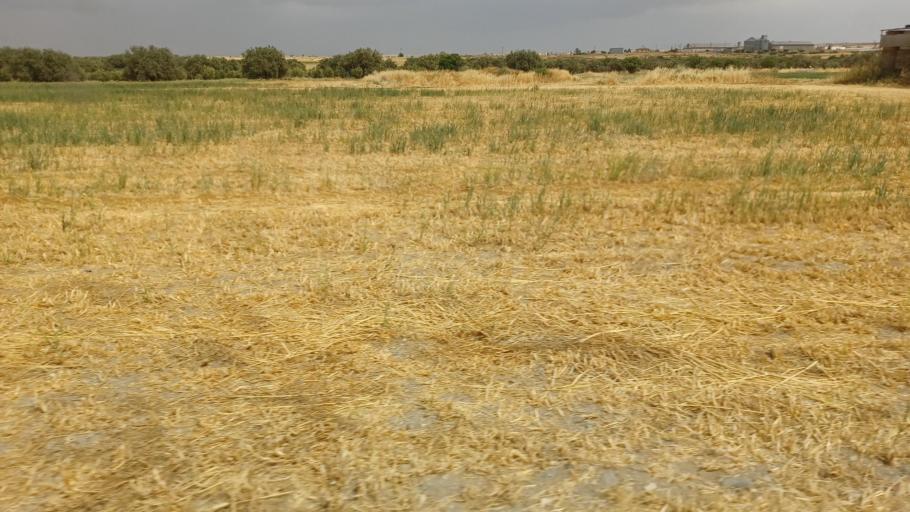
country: CY
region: Larnaka
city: Athienou
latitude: 35.0709
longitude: 33.5226
